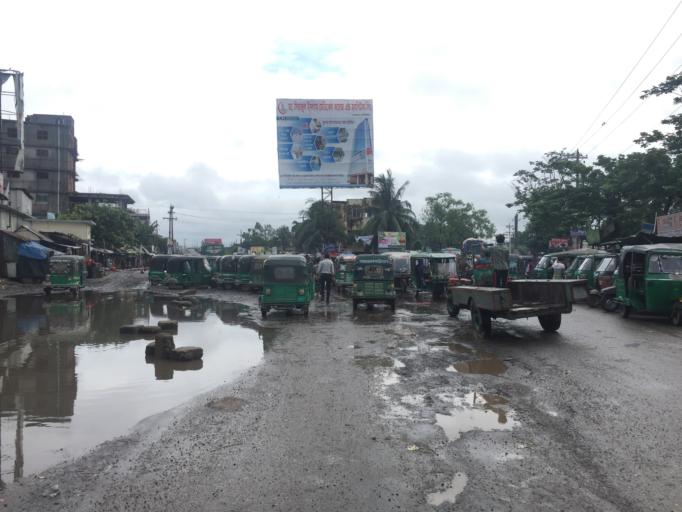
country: BD
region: Dhaka
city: Narayanganj
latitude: 23.5600
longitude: 90.5101
